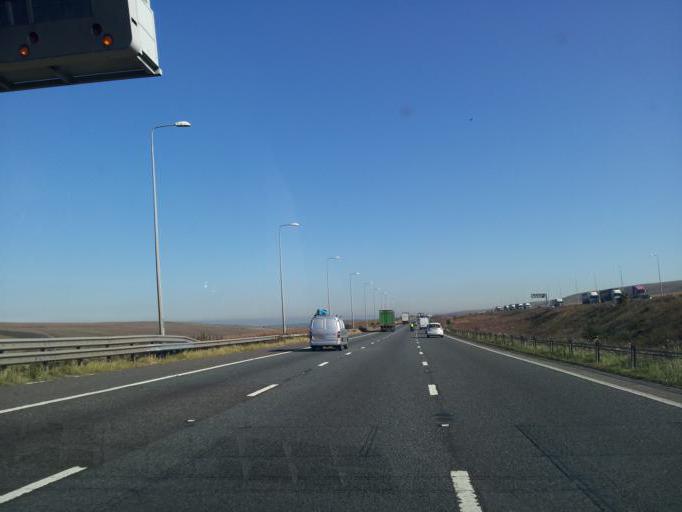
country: GB
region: England
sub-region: Borough of Oldham
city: Diggle
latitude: 53.6321
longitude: -2.0033
